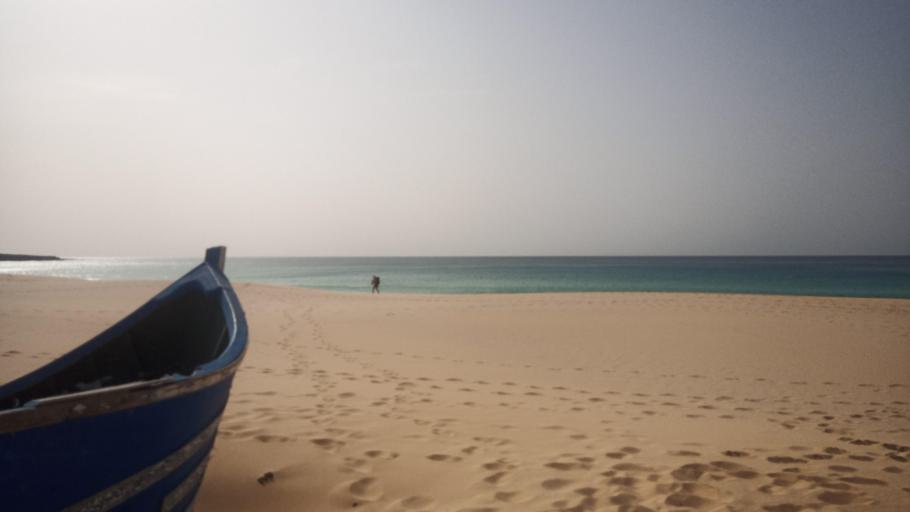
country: ES
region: Canary Islands
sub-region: Provincia de Las Palmas
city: Haria
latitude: 29.2786
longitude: -13.5146
